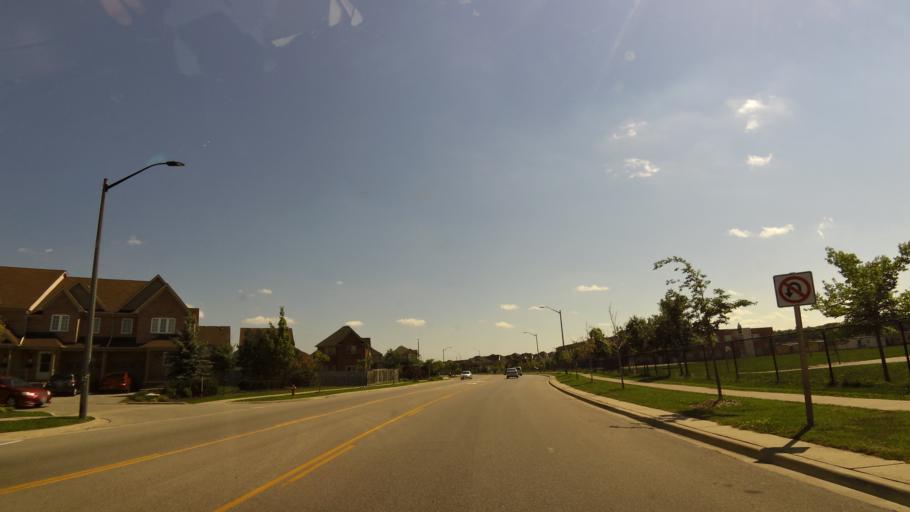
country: CA
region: Ontario
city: Mississauga
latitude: 43.5470
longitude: -79.7271
